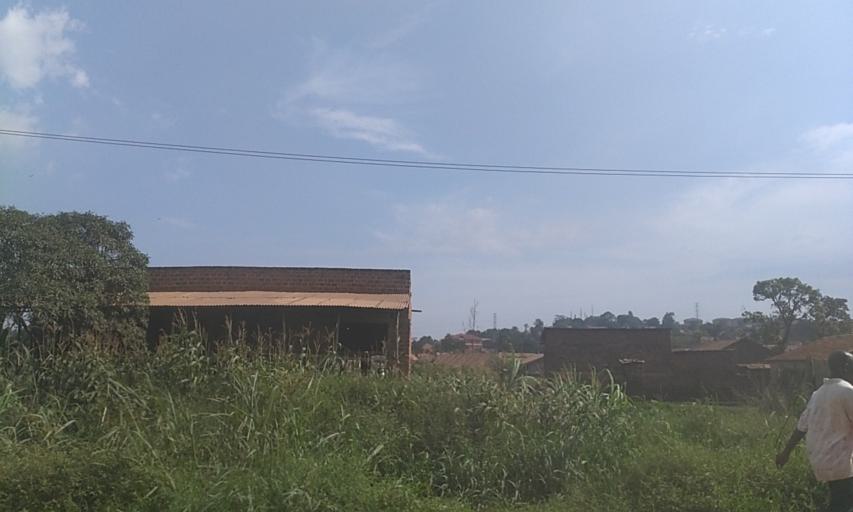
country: UG
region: Central Region
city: Kampala Central Division
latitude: 0.3455
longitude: 32.5444
